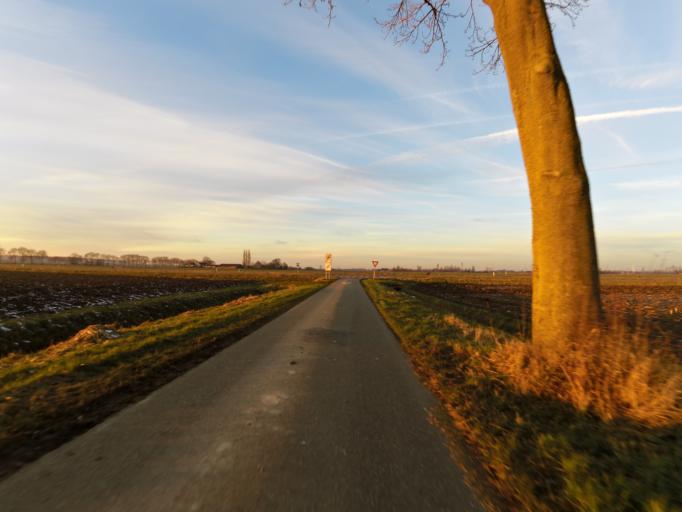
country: NL
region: Gelderland
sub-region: Gemeente Montferland
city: s-Heerenberg
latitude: 51.8976
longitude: 6.2981
